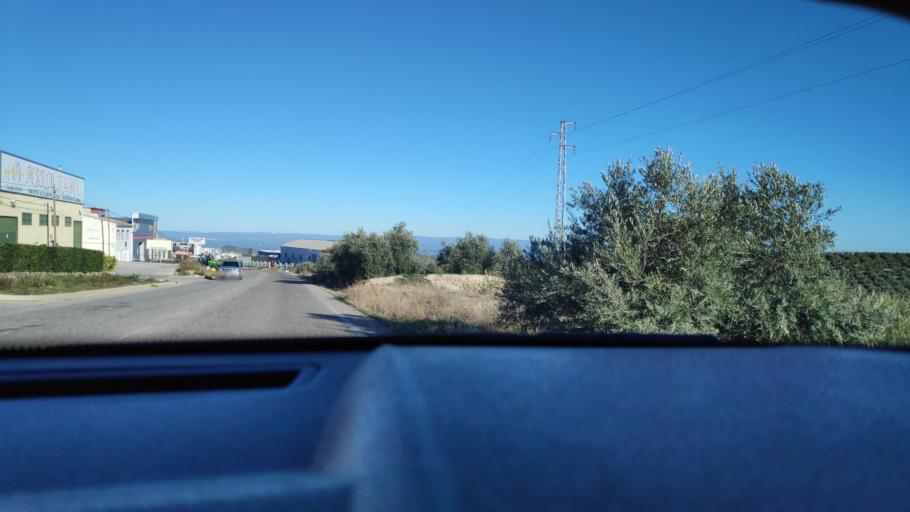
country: ES
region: Andalusia
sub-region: Provincia de Jaen
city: Mancha Real
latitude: 37.7953
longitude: -3.6074
